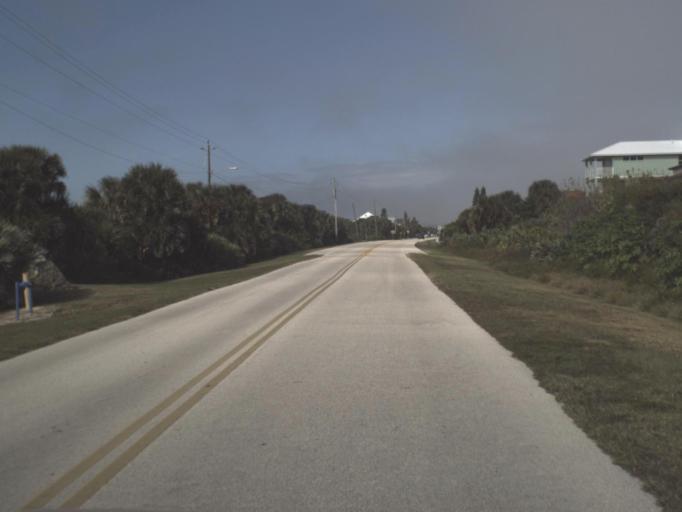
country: US
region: Florida
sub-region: Volusia County
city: Oak Hill
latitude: 28.9383
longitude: -80.8314
